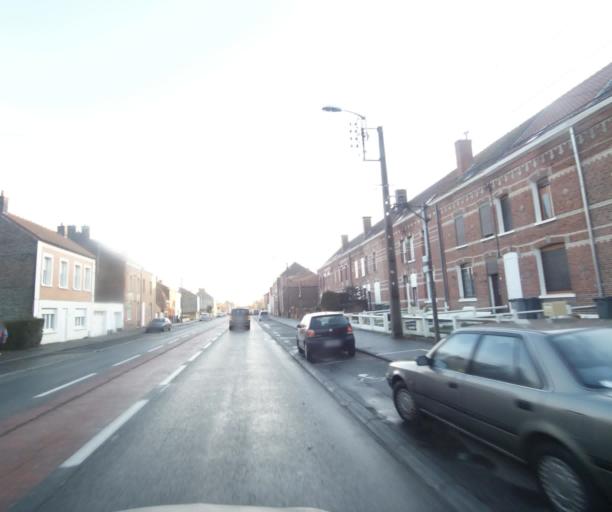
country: FR
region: Nord-Pas-de-Calais
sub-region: Departement du Nord
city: Onnaing
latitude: 50.3883
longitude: 3.6063
